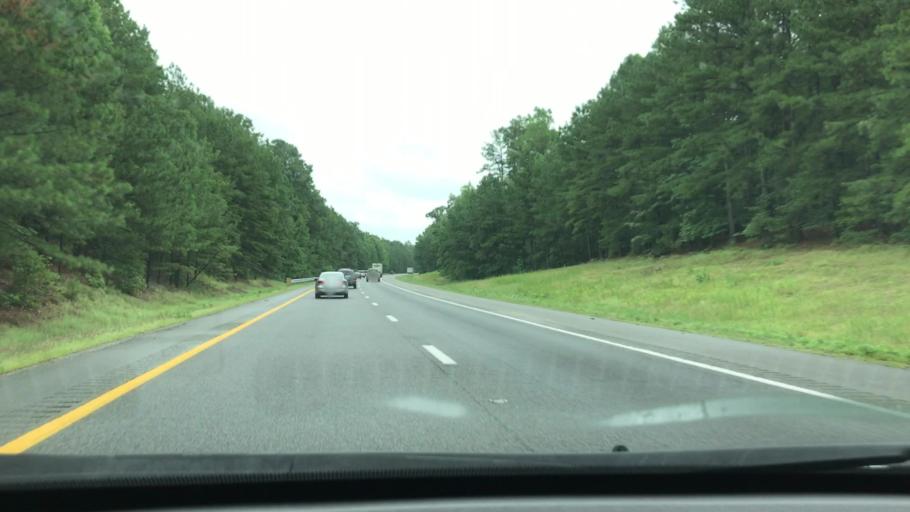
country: US
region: Virginia
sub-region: City of Emporia
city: Emporia
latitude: 36.7511
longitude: -77.5104
